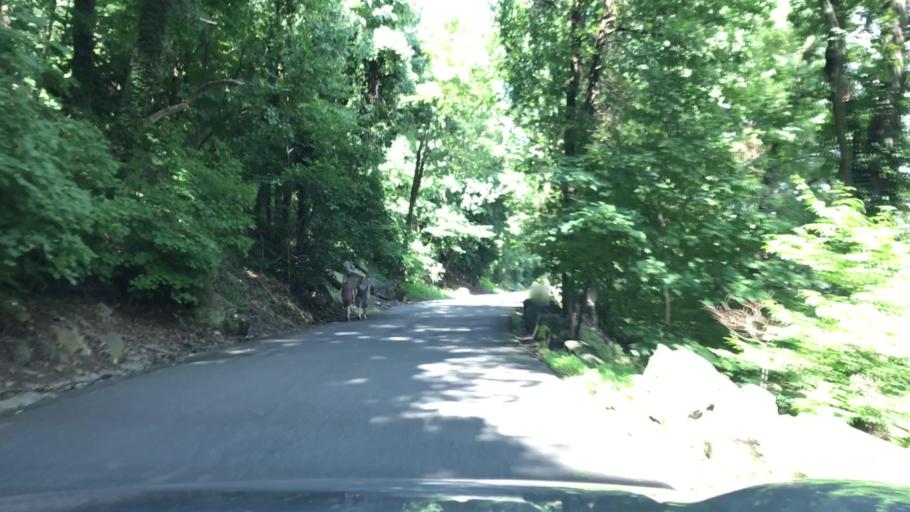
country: US
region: New Jersey
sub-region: Bergen County
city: Englewood Cliffs
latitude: 40.8728
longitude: -73.9491
